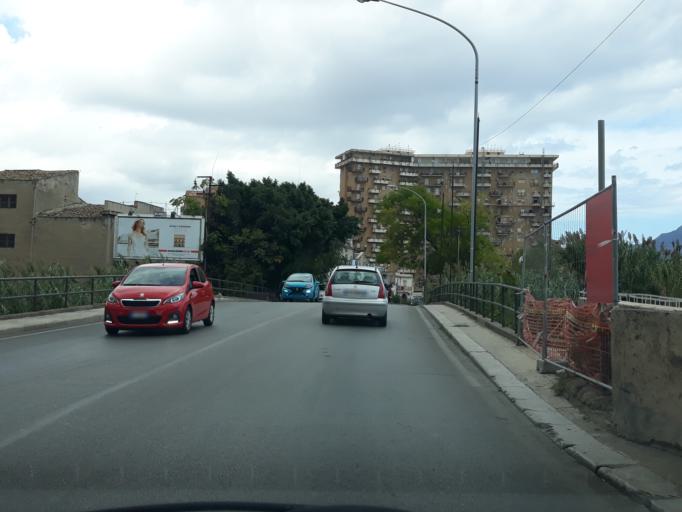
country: IT
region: Sicily
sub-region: Palermo
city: Ciaculli
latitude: 38.1095
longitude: 13.3796
